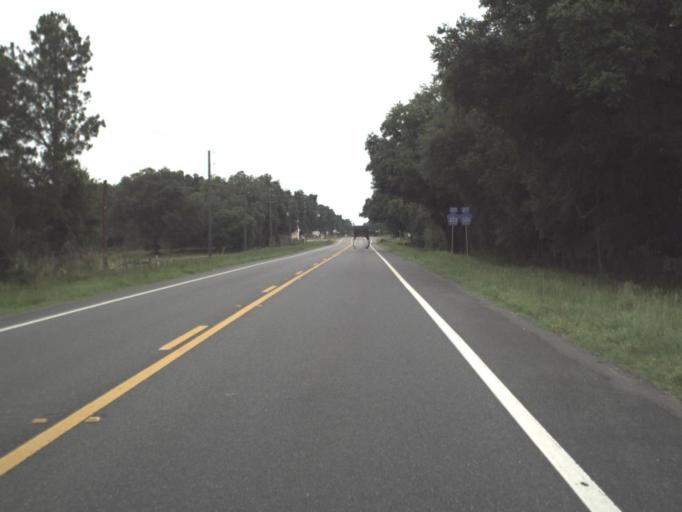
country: US
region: Florida
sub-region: Levy County
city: Williston
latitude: 29.2792
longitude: -82.4443
